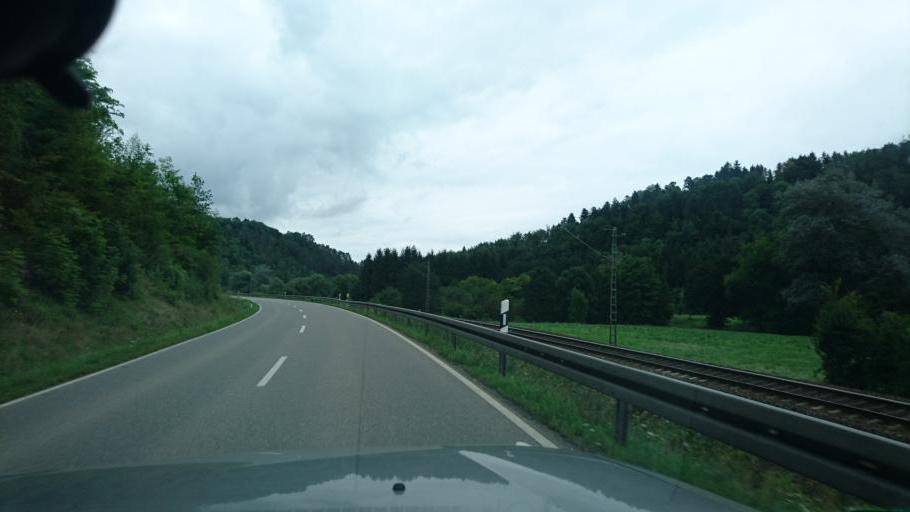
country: DE
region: Baden-Wuerttemberg
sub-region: Freiburg Region
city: Sulz am Neckar
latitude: 48.3710
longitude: 8.6533
